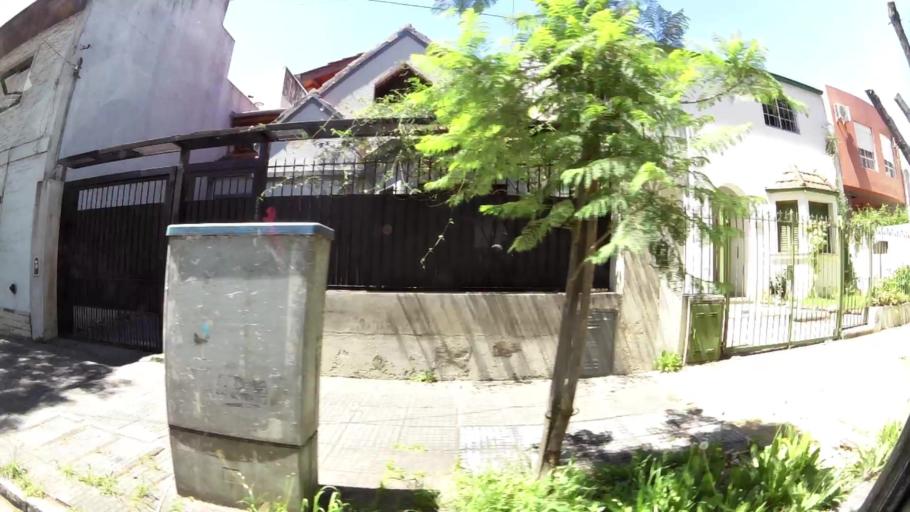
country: AR
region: Buenos Aires
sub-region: Partido de Vicente Lopez
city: Olivos
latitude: -34.5113
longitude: -58.4989
